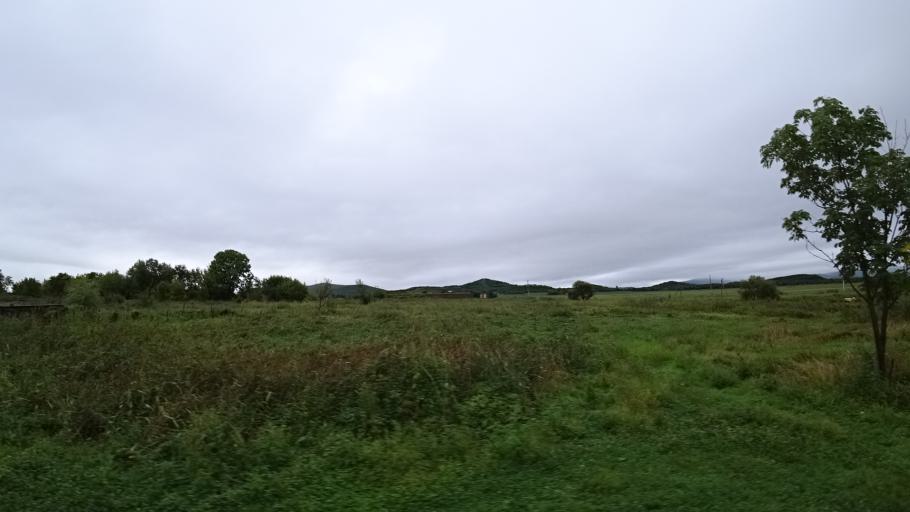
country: RU
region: Primorskiy
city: Monastyrishche
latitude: 44.2268
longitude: 132.4573
